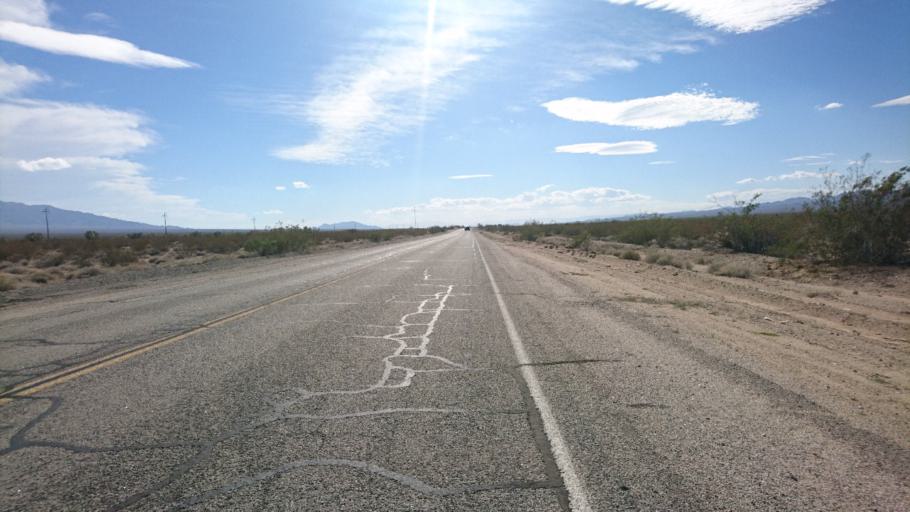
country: US
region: California
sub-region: San Bernardino County
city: Needles
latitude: 34.7478
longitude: -115.2327
